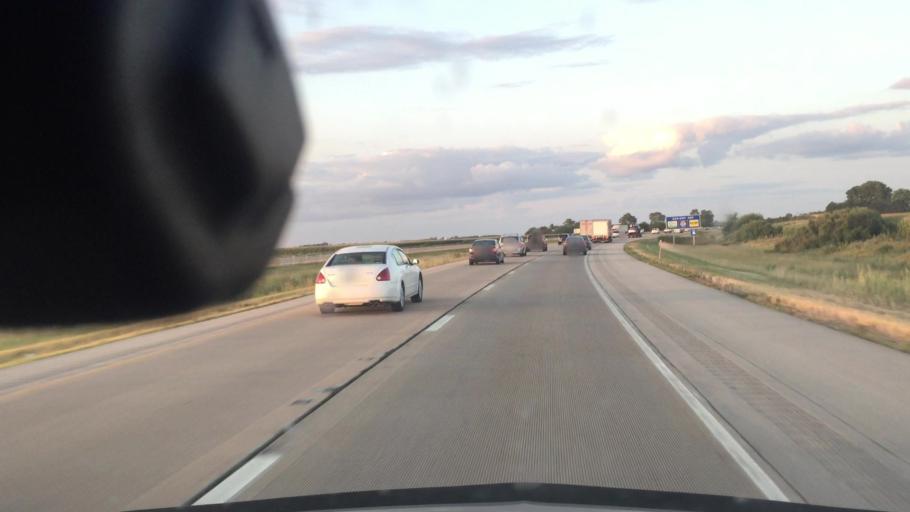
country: US
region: Illinois
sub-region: Livingston County
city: Dwight
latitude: 41.1108
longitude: -88.4437
